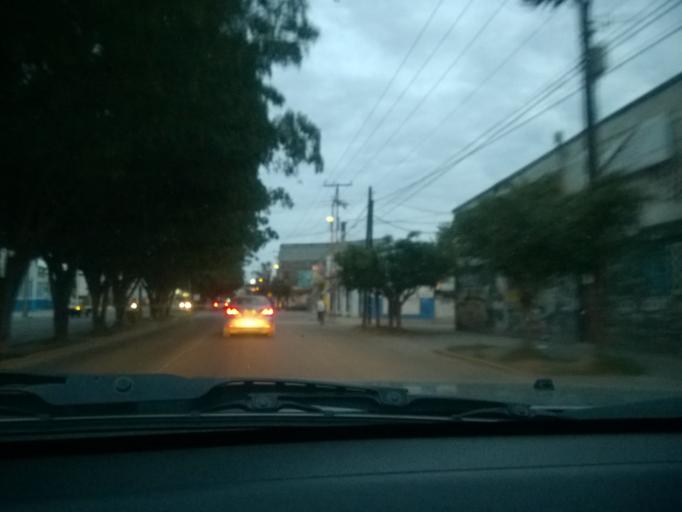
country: MX
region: Guanajuato
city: Leon
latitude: 21.1302
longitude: -101.6548
